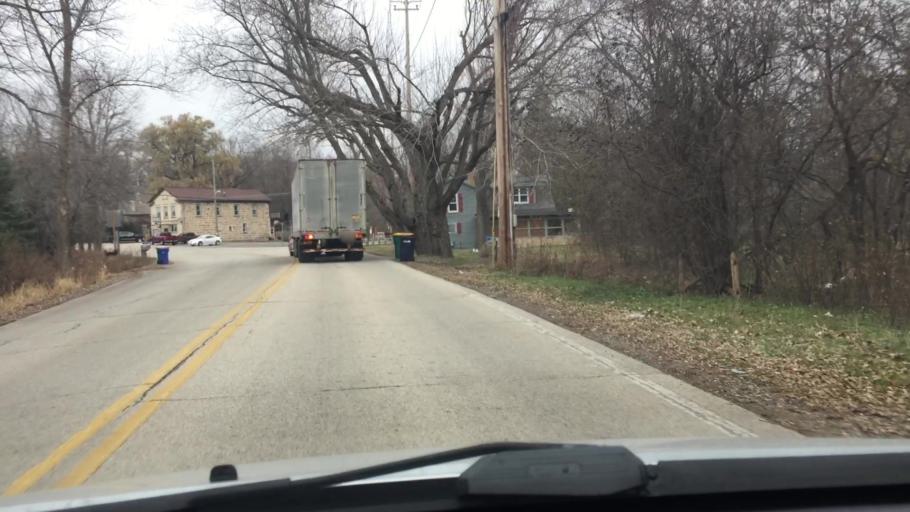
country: US
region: Wisconsin
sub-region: Ozaukee County
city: Cedarburg
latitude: 43.2830
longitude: -87.9717
